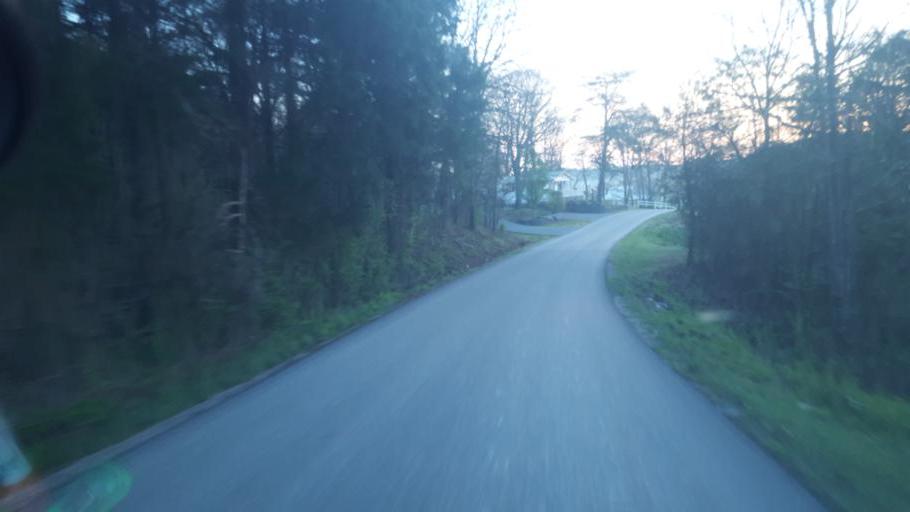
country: US
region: Kentucky
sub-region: Hart County
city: Munfordville
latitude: 37.2629
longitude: -85.9688
